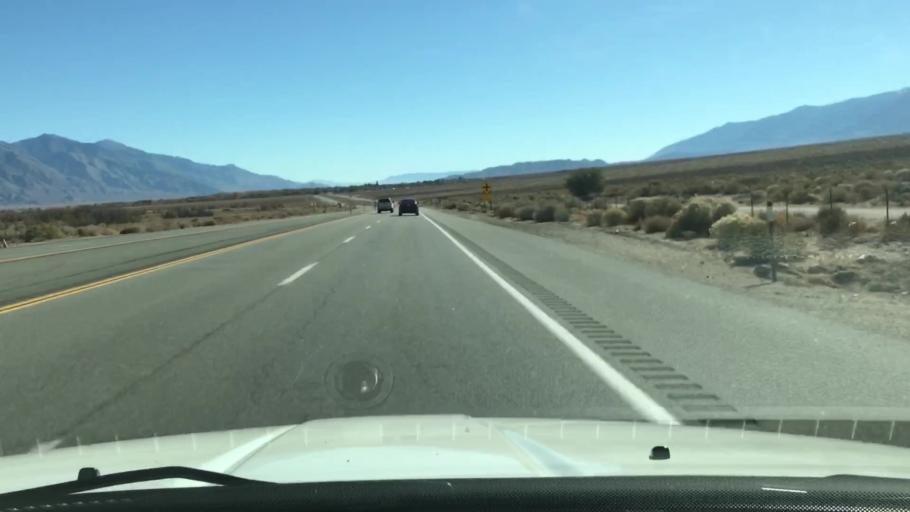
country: US
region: California
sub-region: Inyo County
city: Lone Pine
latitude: 36.8323
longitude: -118.2267
